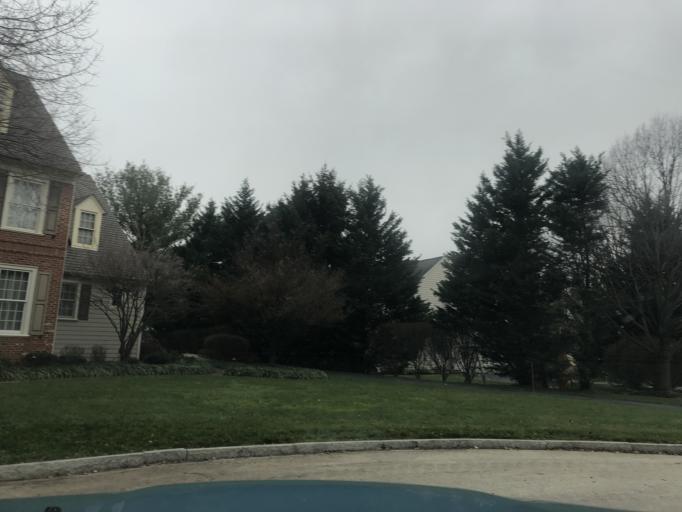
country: US
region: Pennsylvania
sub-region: Delaware County
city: Radnor
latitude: 40.0291
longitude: -75.3535
